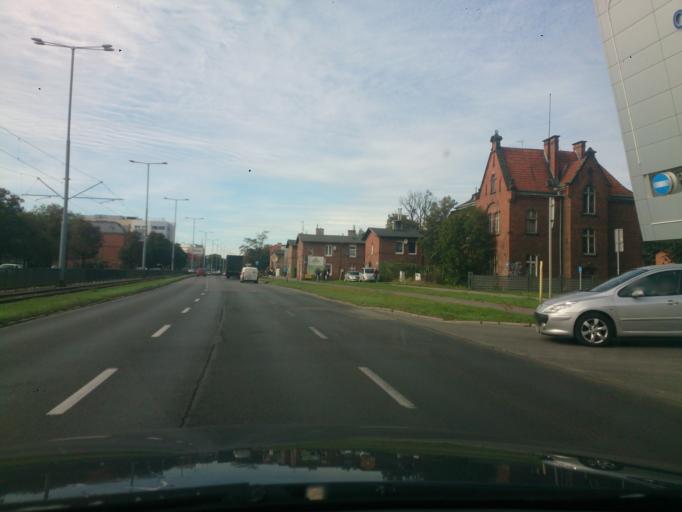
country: PL
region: Pomeranian Voivodeship
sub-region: Gdansk
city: Gdansk
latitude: 54.3839
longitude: 18.5963
